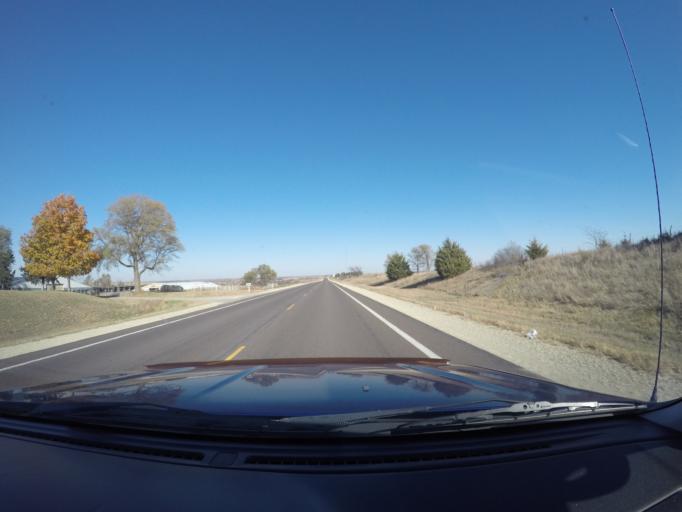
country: US
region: Kansas
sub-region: Marshall County
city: Blue Rapids
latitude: 39.6717
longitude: -96.7507
